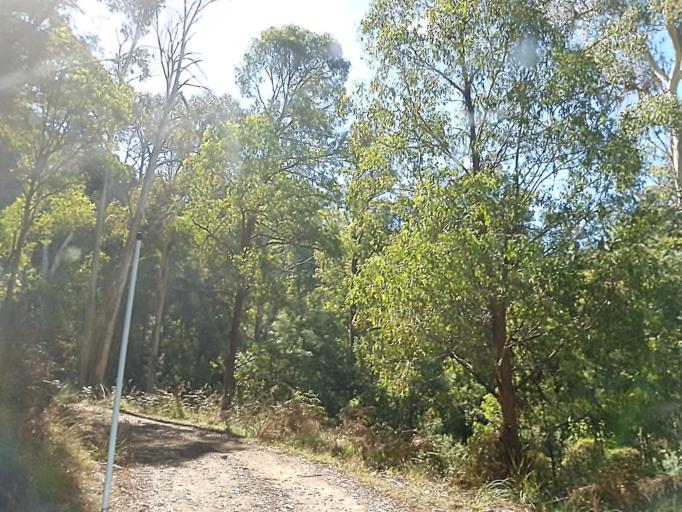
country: AU
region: Victoria
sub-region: Alpine
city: Mount Beauty
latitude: -36.8826
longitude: 147.0299
